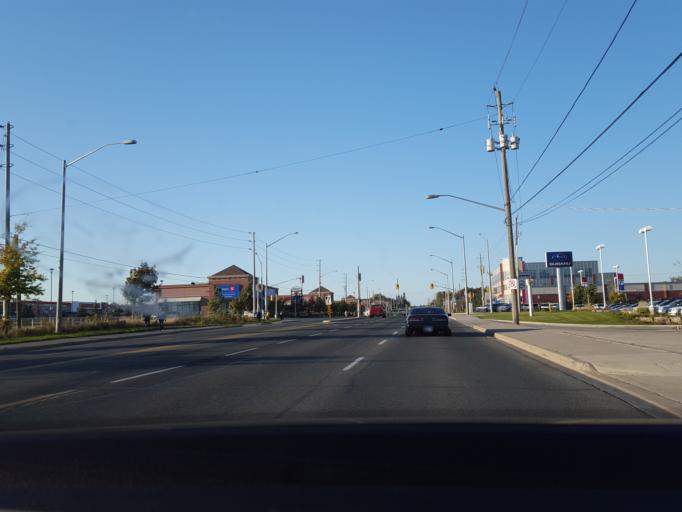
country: CA
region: Ontario
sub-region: York
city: Richmond Hill
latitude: 43.9106
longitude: -79.4463
